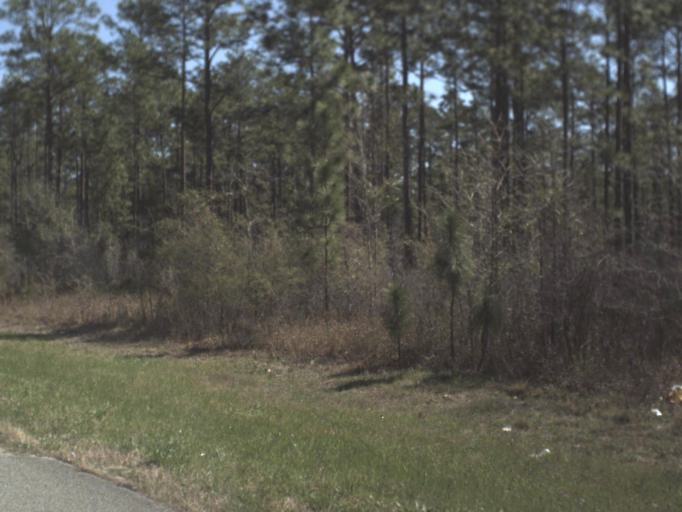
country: US
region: Florida
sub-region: Leon County
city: Woodville
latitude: 30.3386
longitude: -84.3199
